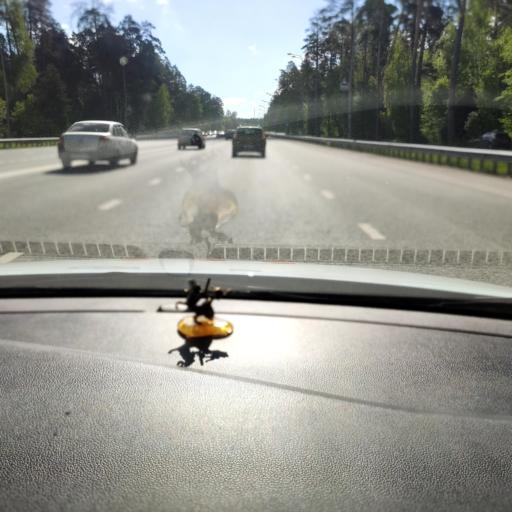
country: RU
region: Tatarstan
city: Staroye Arakchino
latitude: 55.8398
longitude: 48.9692
